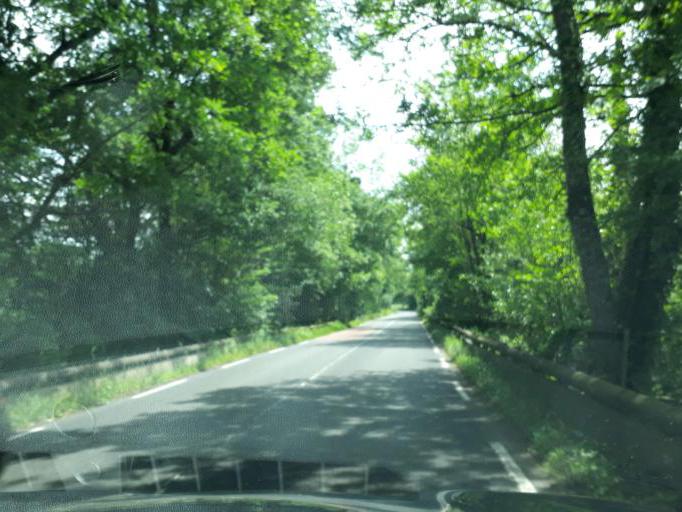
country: FR
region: Centre
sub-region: Departement du Loiret
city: Sandillon
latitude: 47.8100
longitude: 2.0534
